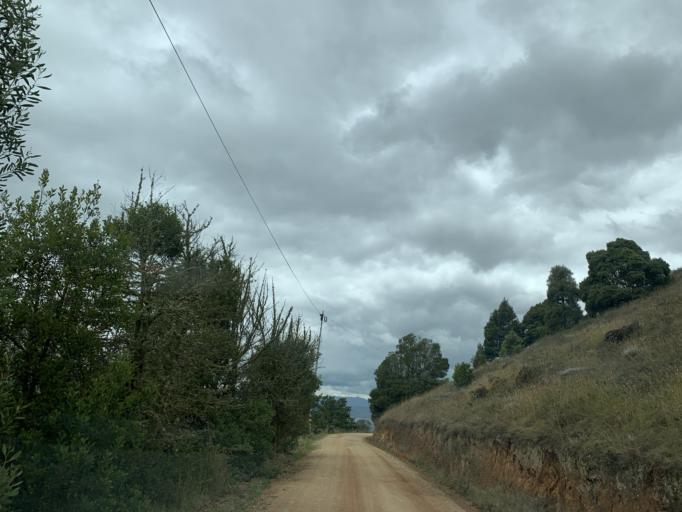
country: CO
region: Boyaca
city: Tunja
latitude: 5.5429
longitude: -73.3215
